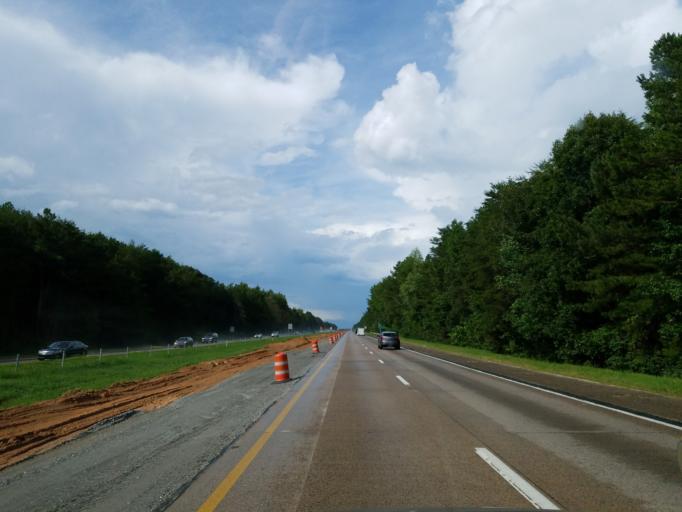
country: US
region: Georgia
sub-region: Forsyth County
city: Cumming
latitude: 34.2405
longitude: -84.0974
